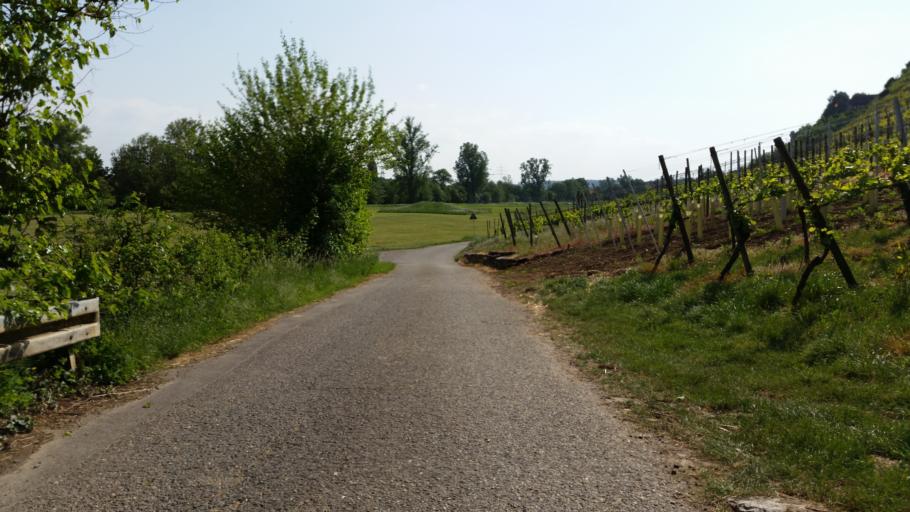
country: DE
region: Baden-Wuerttemberg
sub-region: Regierungsbezirk Stuttgart
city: Pleidelsheim
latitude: 48.9758
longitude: 9.2072
